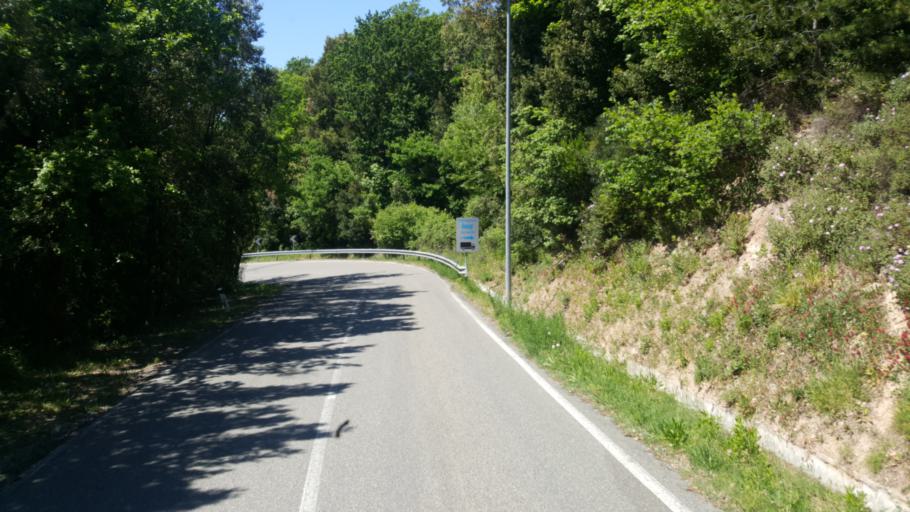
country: IT
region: Tuscany
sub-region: Province of Pisa
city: Castellina Marittima
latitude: 43.4239
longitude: 10.5445
